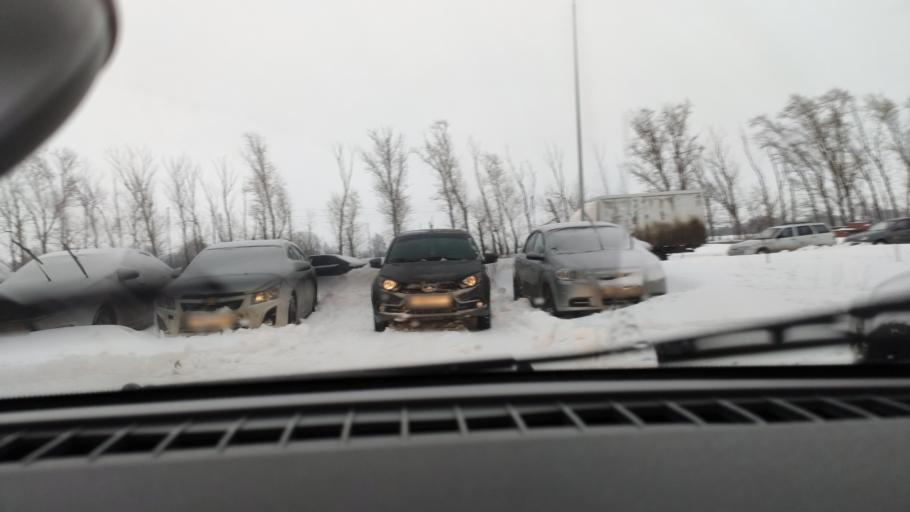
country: RU
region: Samara
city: Samara
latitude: 53.0920
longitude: 50.1611
